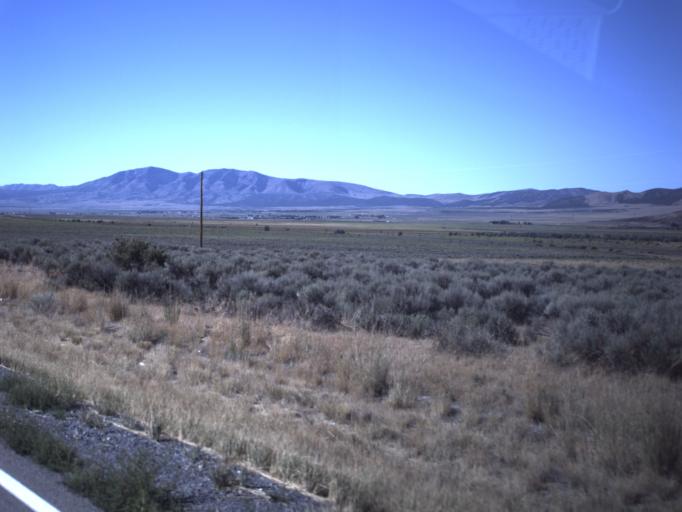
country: US
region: Utah
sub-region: Tooele County
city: Tooele
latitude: 40.4082
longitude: -112.3850
